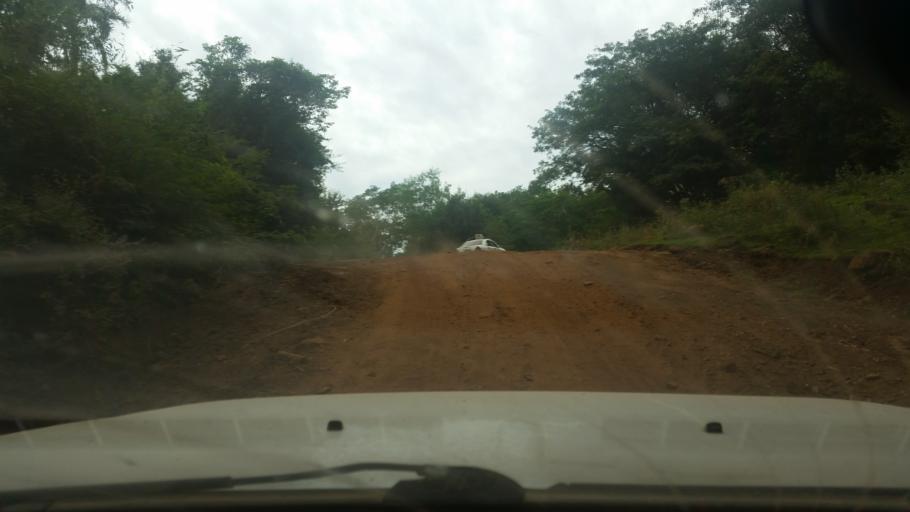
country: PY
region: Guaira
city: Independencia
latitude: -25.8189
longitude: -56.2752
